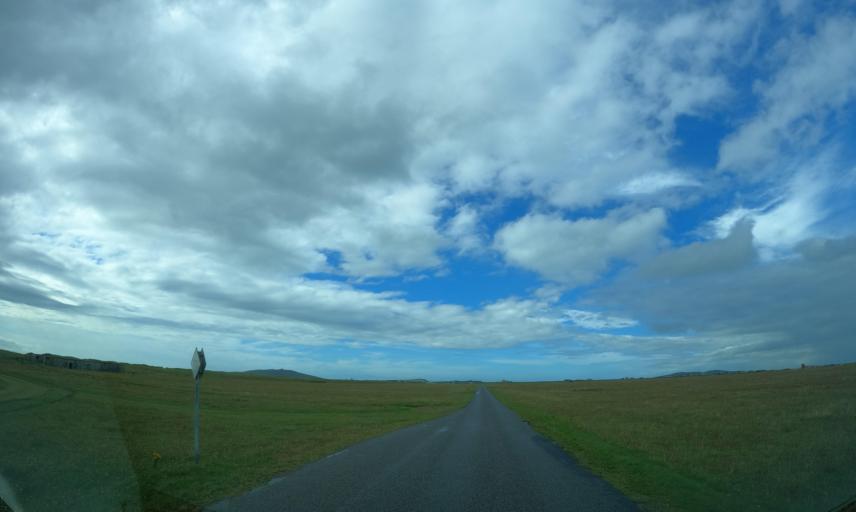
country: GB
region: Scotland
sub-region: Eilean Siar
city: Barra
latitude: 56.4937
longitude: -6.8628
